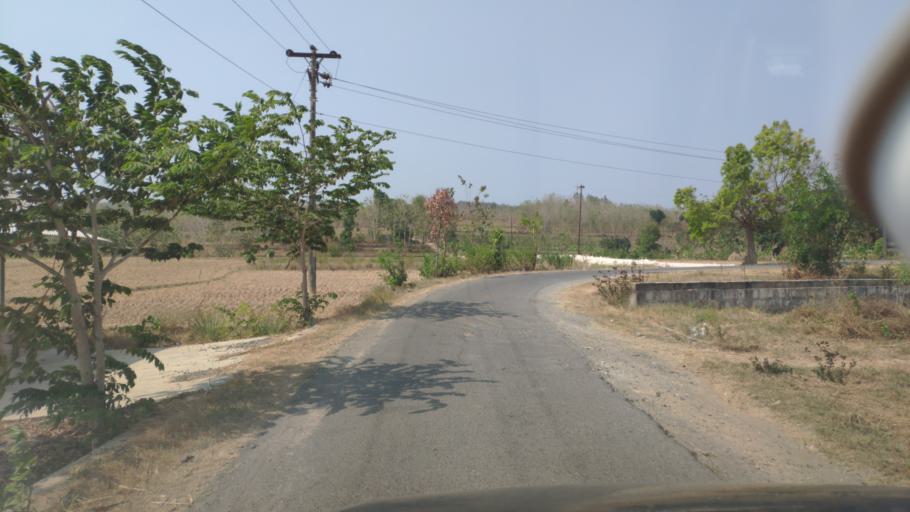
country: ID
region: Central Java
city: Tempuran
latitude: -6.9125
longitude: 111.4557
